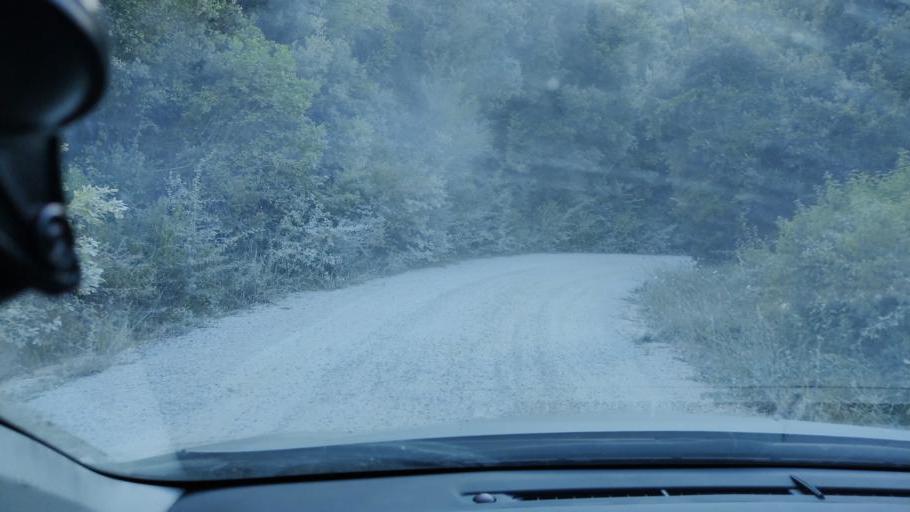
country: IT
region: Umbria
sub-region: Provincia di Terni
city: Amelia
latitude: 42.5406
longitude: 12.3824
